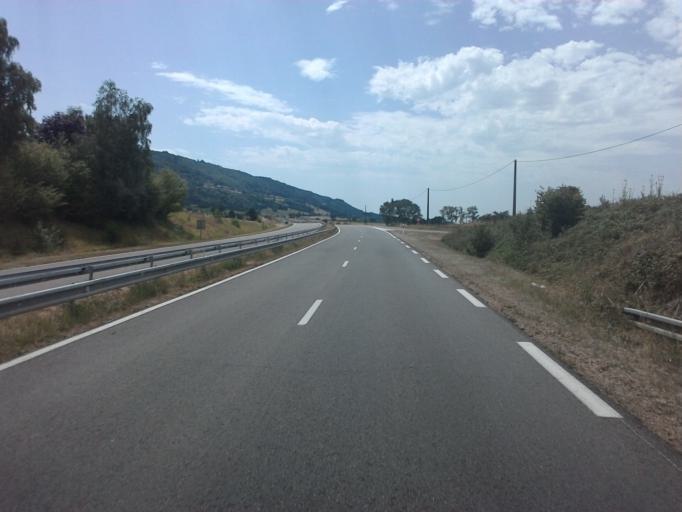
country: FR
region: Franche-Comte
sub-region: Departement du Jura
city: Saint-Amour
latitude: 46.4233
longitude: 5.3499
